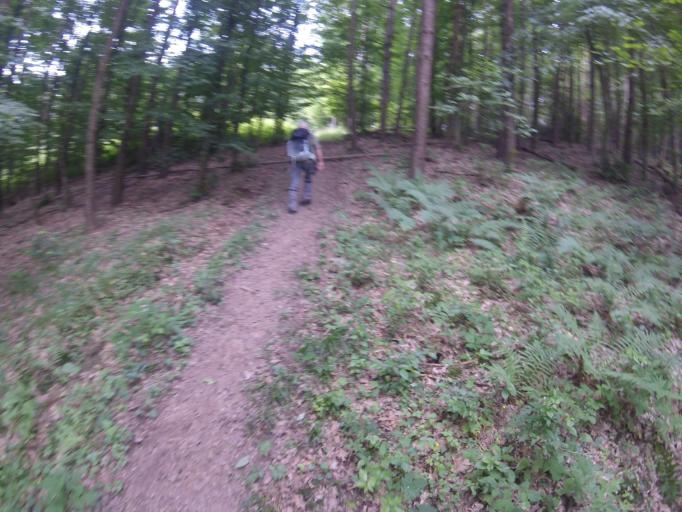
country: SI
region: Hodos-Hodos
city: Hodos
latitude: 46.8493
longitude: 16.4390
